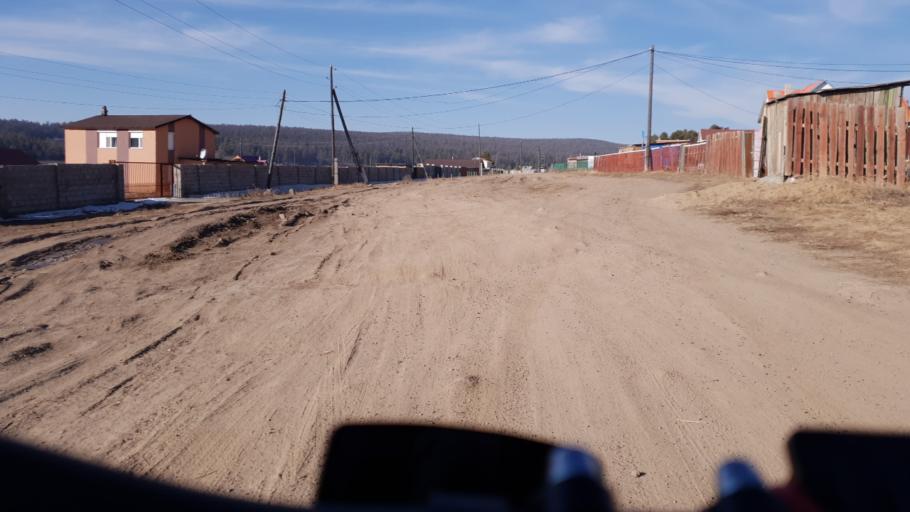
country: MN
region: Ulaanbaatar
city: Ulaanbaatar
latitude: 48.1516
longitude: 106.8850
